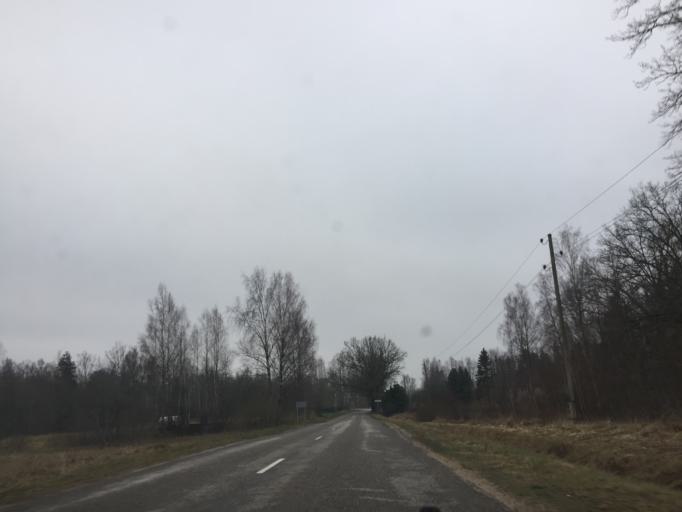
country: LV
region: Limbazu Rajons
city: Limbazi
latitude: 57.5227
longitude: 24.6887
